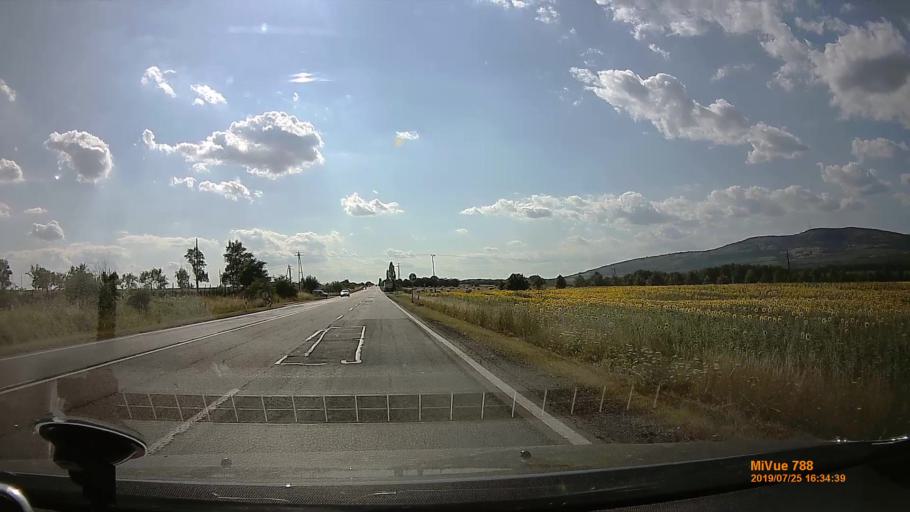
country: HU
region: Heves
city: Abasar
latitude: 47.7674
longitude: 20.0193
